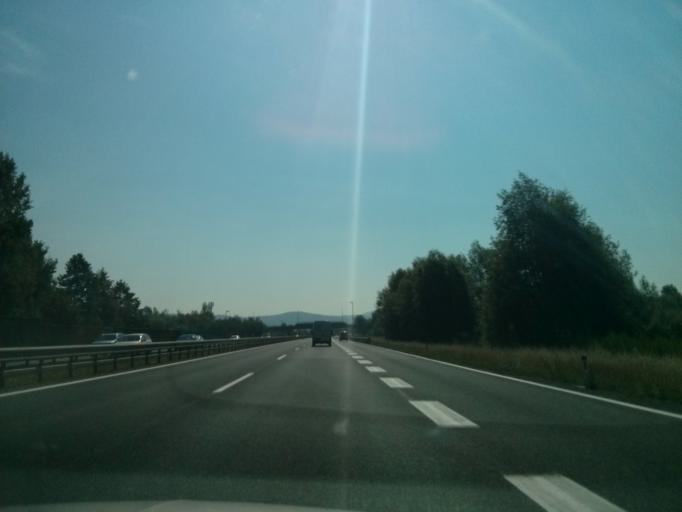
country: SI
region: Ljubljana
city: Ljubljana
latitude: 46.0261
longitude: 14.4942
